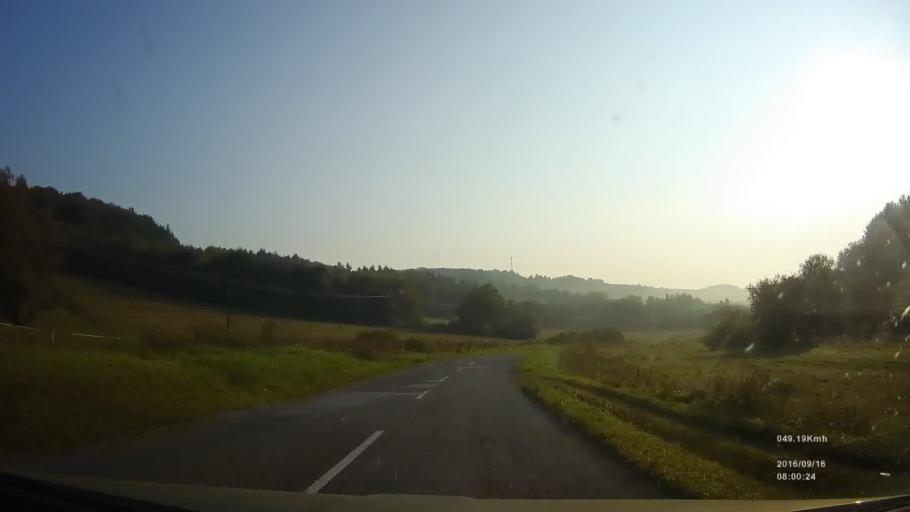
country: SK
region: Presovsky
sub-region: Okres Presov
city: Presov
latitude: 48.9164
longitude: 21.1583
